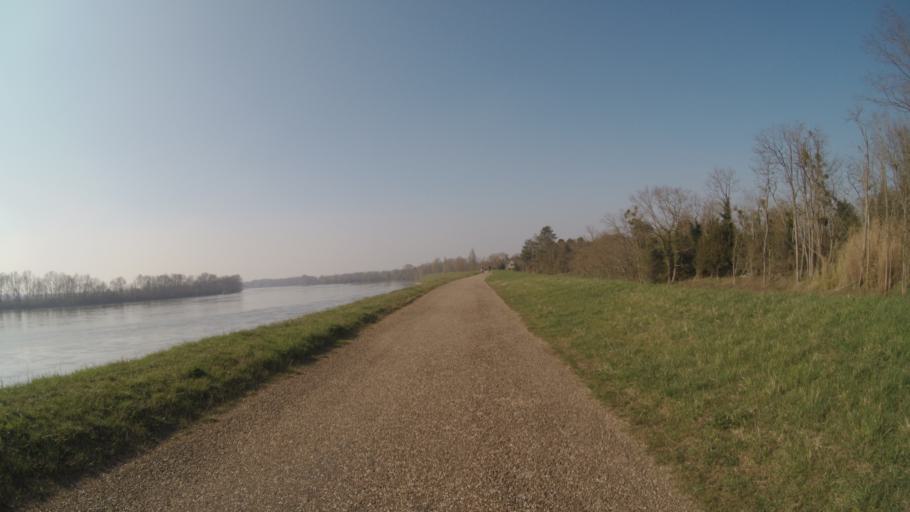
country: FR
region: Centre
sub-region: Departement du Loiret
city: Checy
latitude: 47.8800
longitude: 2.0342
